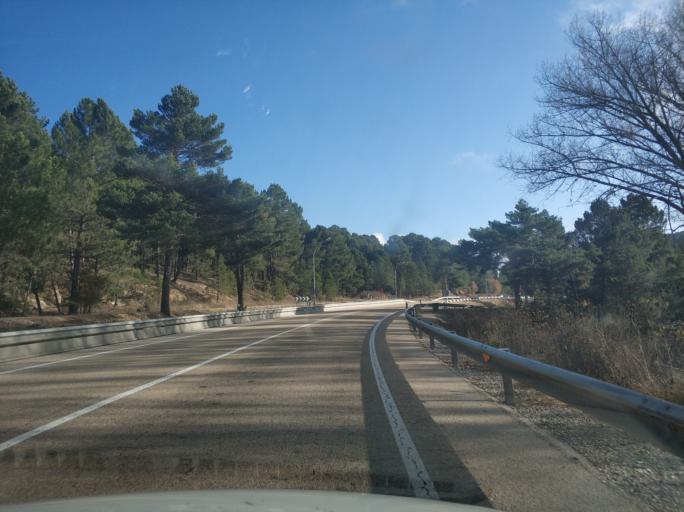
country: ES
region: Castille and Leon
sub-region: Provincia de Soria
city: San Leonardo de Yague
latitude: 41.8329
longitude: -3.0544
